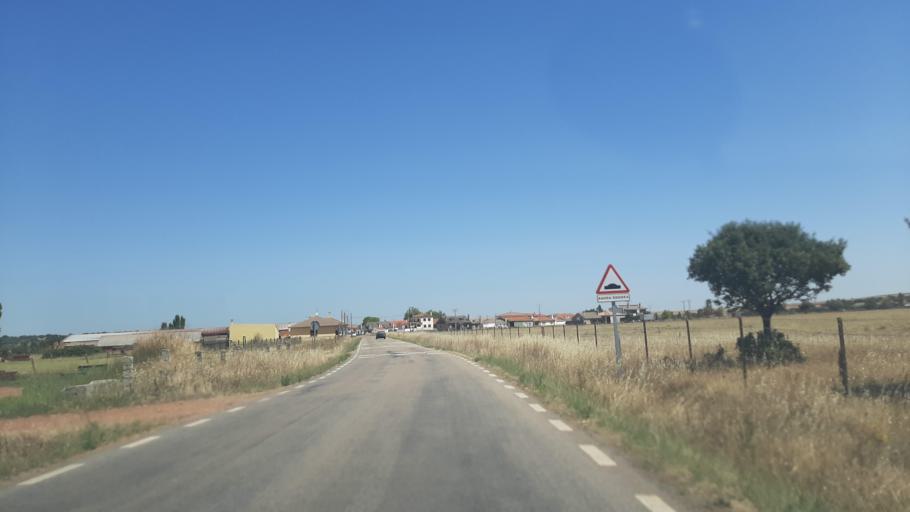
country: ES
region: Castille and Leon
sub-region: Provincia de Salamanca
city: Cabrillas
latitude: 40.7335
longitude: -6.1774
